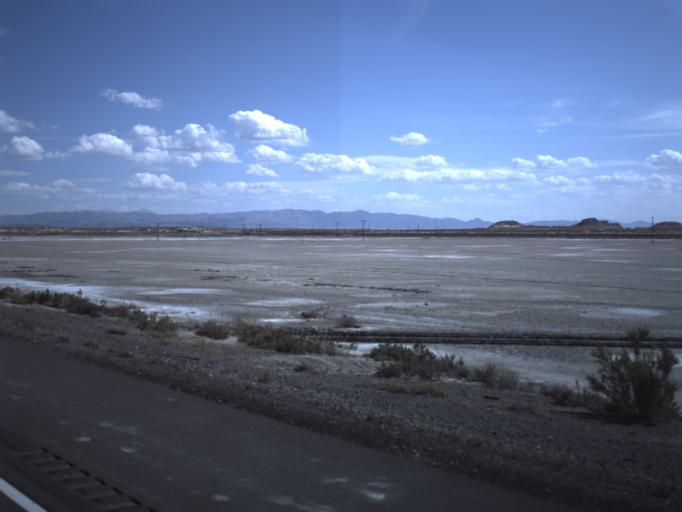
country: US
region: Utah
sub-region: Tooele County
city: Wendover
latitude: 40.7271
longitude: -113.2956
